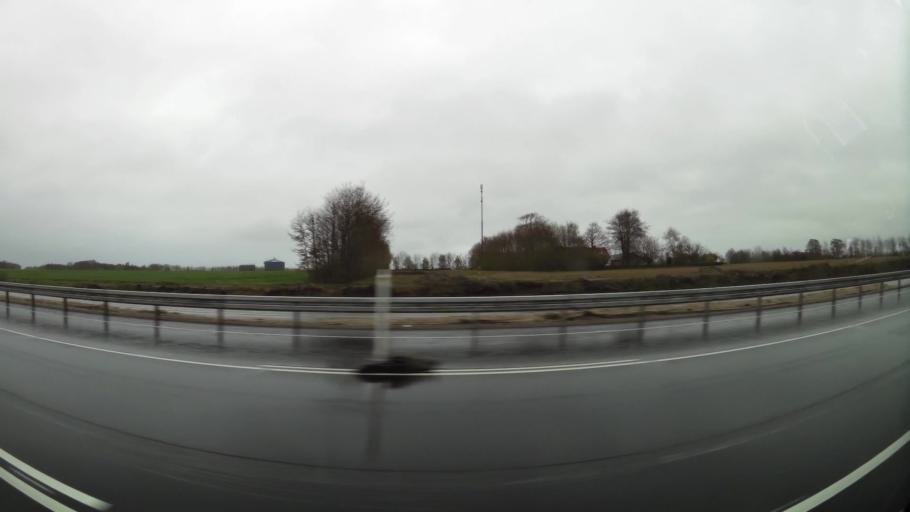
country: DK
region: Central Jutland
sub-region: Herning Kommune
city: Snejbjerg
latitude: 56.2037
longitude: 8.8737
